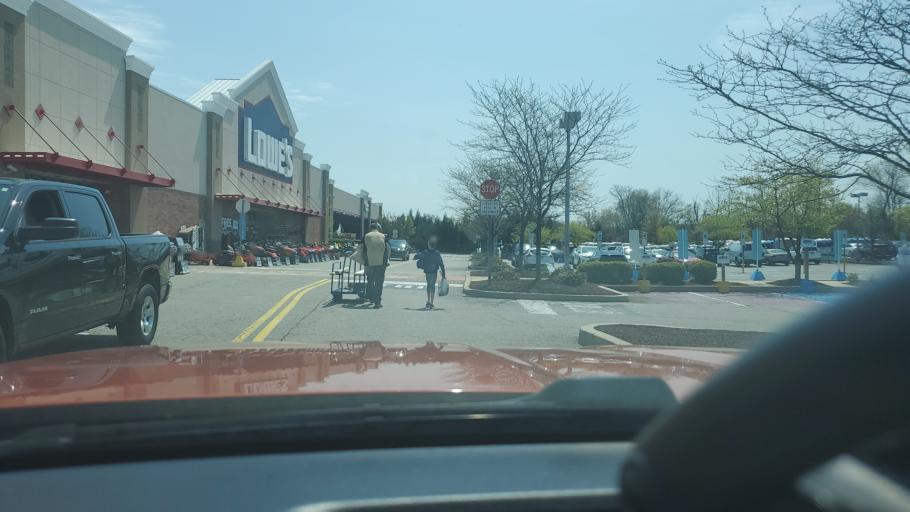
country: US
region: Pennsylvania
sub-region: Chester County
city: South Pottstown
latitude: 40.2254
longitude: -75.6588
